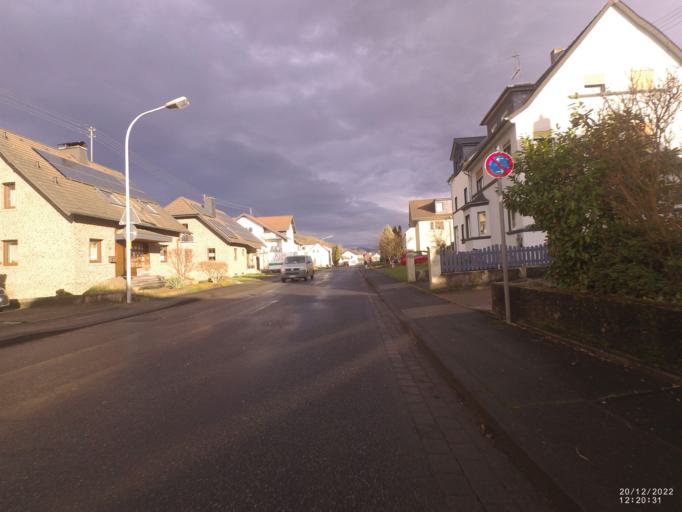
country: DE
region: Rheinland-Pfalz
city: Sinzig
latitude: 50.5395
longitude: 7.2341
